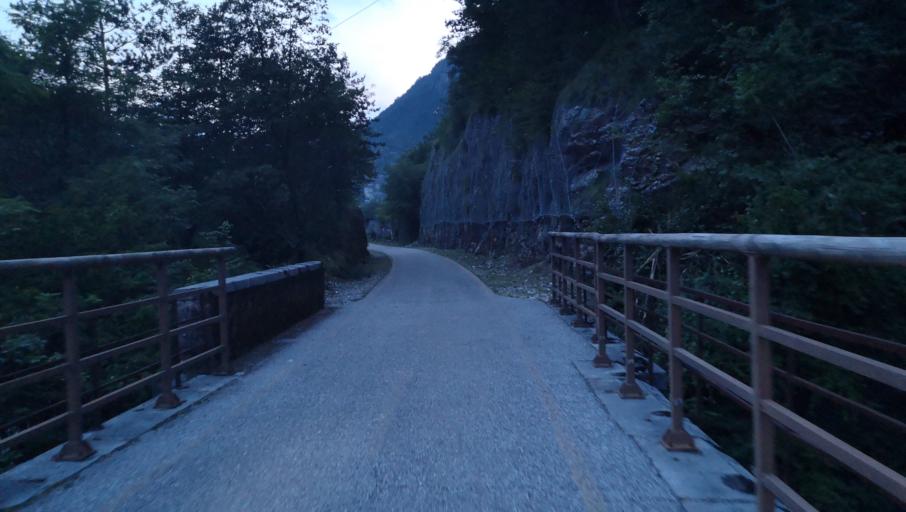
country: IT
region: Friuli Venezia Giulia
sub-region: Provincia di Udine
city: Chiusaforte
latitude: 46.3965
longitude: 13.2713
